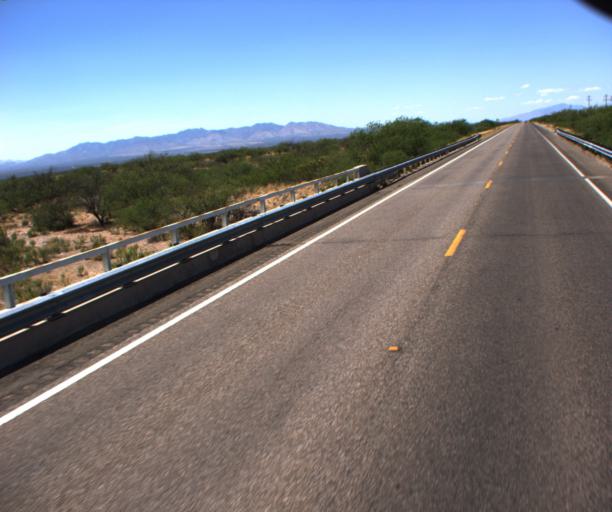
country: US
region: Arizona
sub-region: Cochise County
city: Tombstone
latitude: 31.7598
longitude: -110.1108
